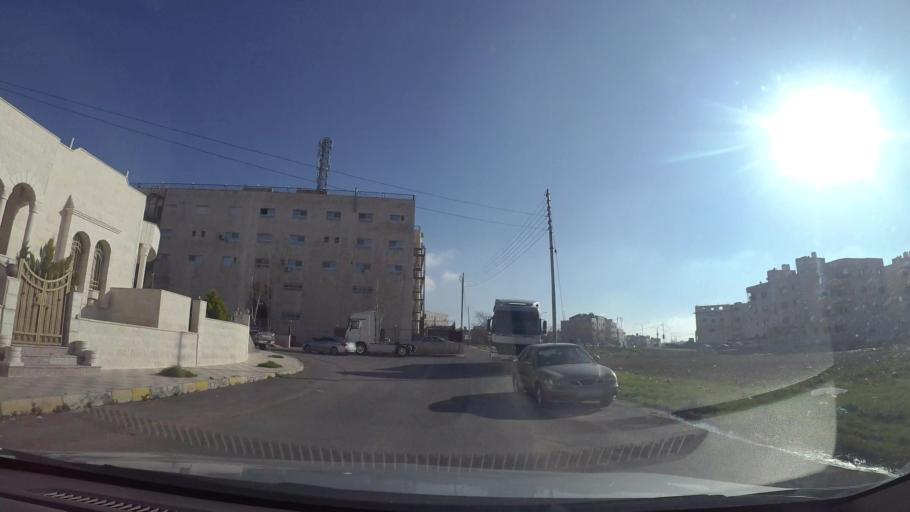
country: JO
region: Amman
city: Al Quwaysimah
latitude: 31.9015
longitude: 35.9273
